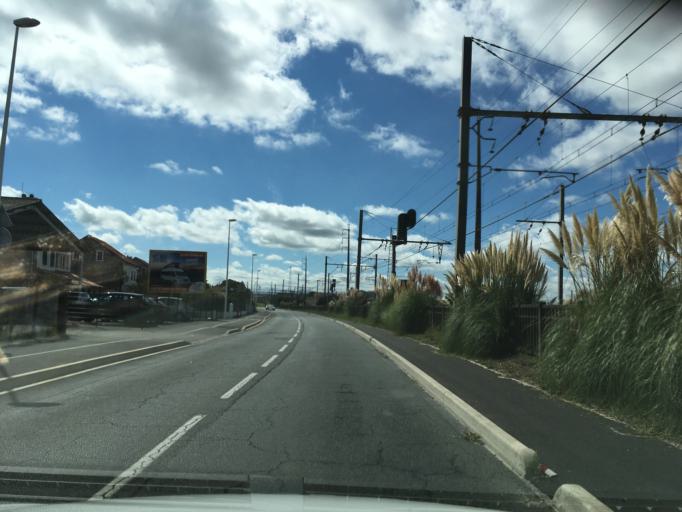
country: FR
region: Aquitaine
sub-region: Departement des Pyrenees-Atlantiques
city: Bayonne
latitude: 43.5104
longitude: -1.4872
